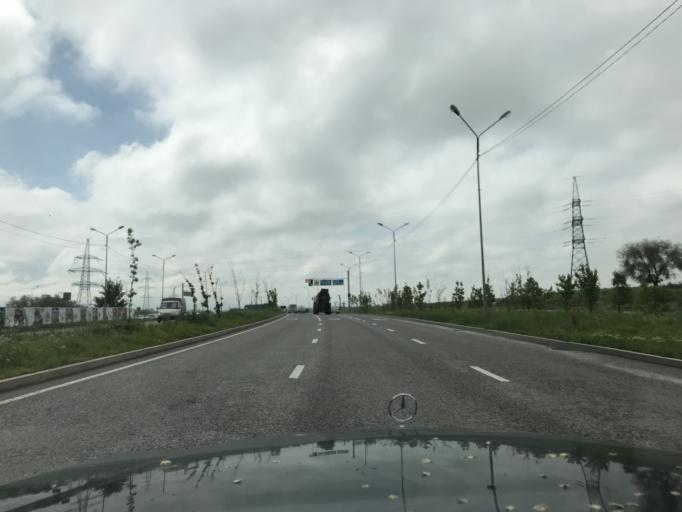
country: KZ
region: Almaty Oblysy
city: Burunday
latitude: 43.2822
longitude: 76.8176
